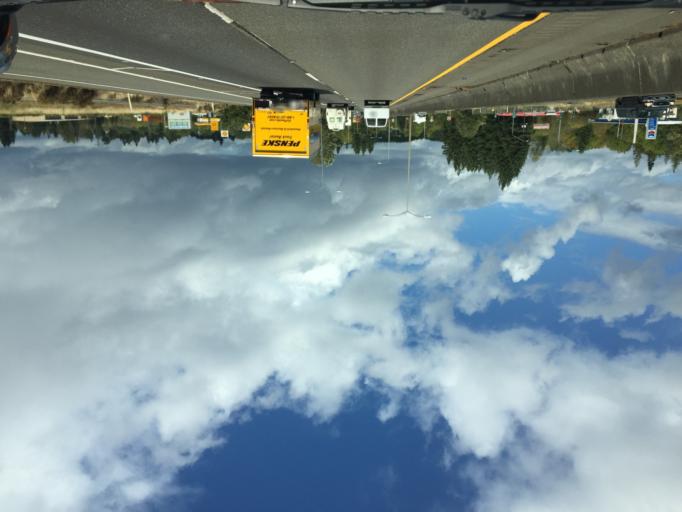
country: US
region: Washington
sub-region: Lewis County
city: Winlock
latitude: 46.4162
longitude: -122.8905
